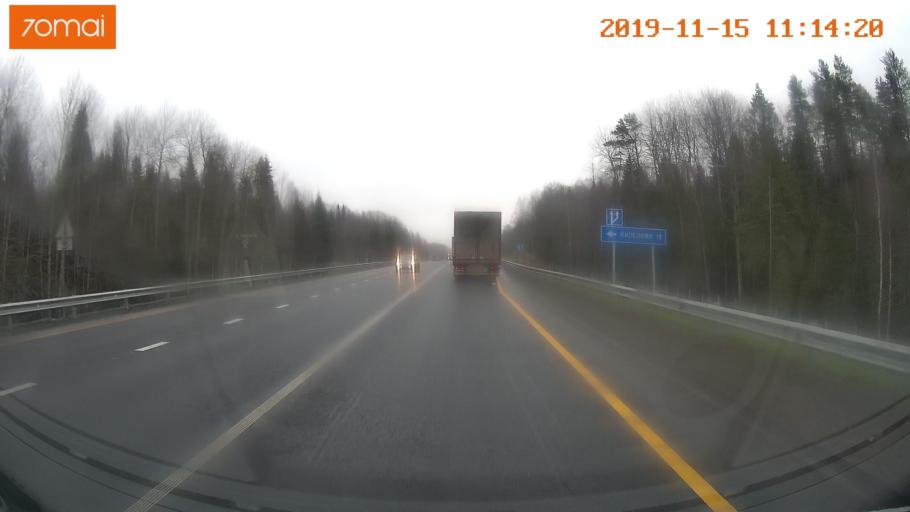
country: RU
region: Vologda
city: Chebsara
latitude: 59.1245
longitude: 39.1862
